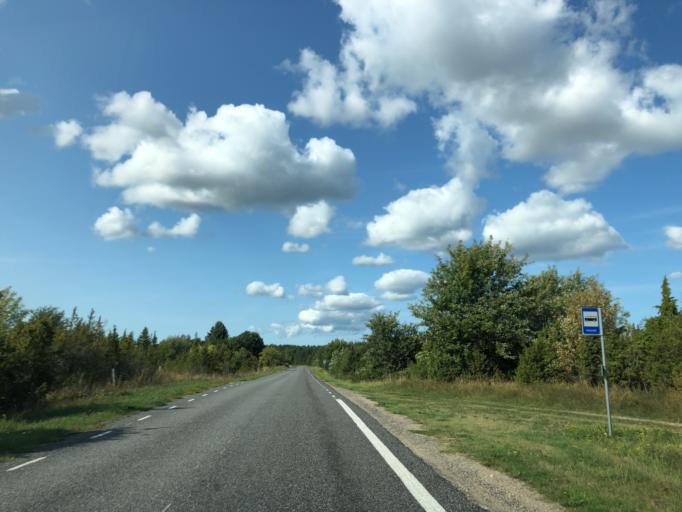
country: EE
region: Hiiumaa
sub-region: Kaerdla linn
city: Kardla
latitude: 58.8022
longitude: 22.7470
